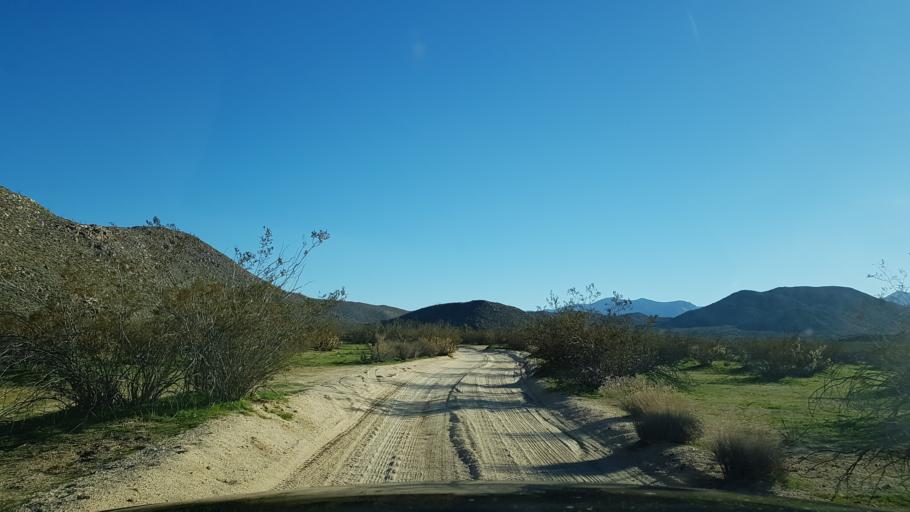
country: US
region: California
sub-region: San Diego County
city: Julian
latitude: 33.0235
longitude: -116.3953
